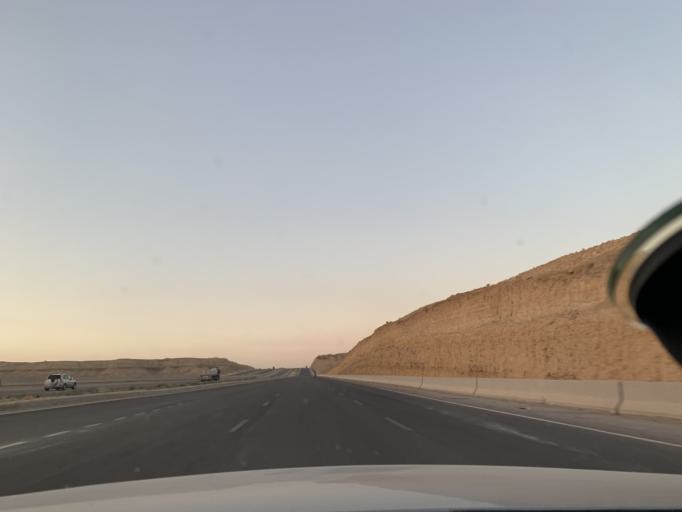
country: EG
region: Muhafazat al Qahirah
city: Halwan
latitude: 29.9436
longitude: 31.5335
